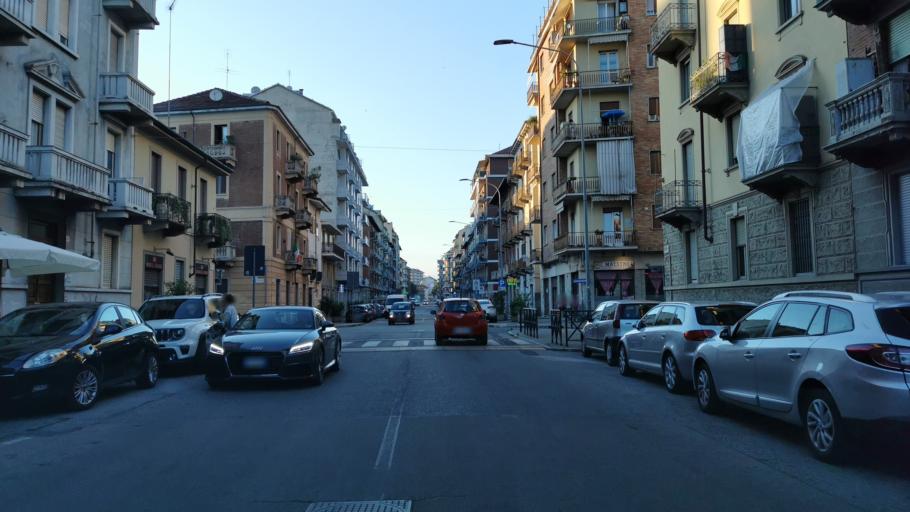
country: IT
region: Piedmont
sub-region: Provincia di Torino
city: Turin
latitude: 45.0958
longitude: 7.6938
